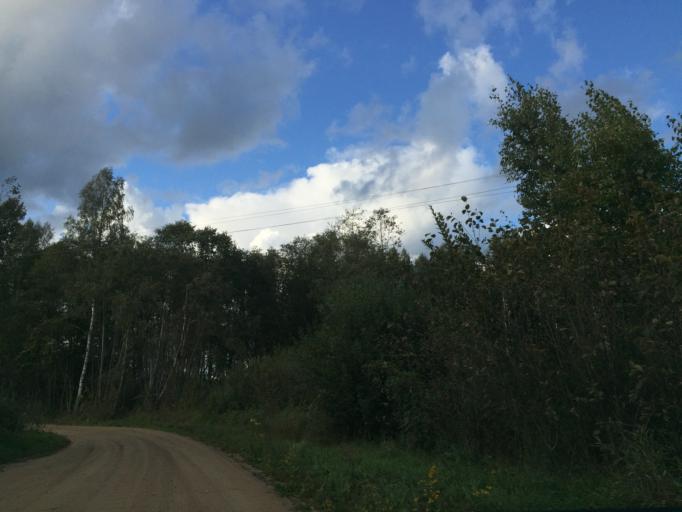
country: LV
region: Ligatne
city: Ligatne
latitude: 57.1347
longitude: 25.0982
